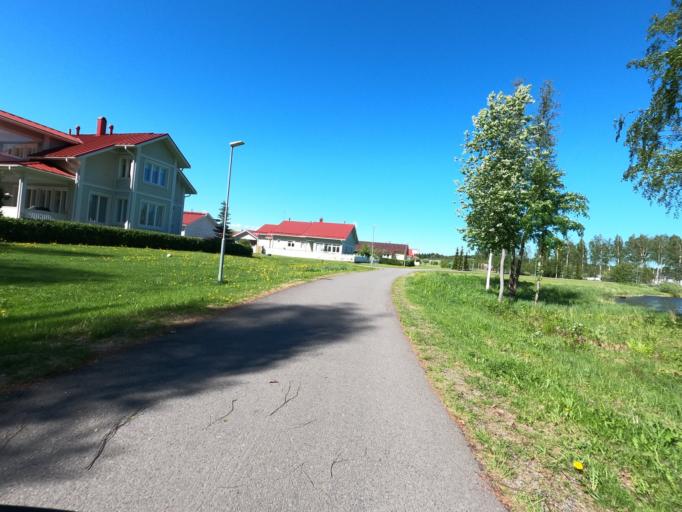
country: FI
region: North Karelia
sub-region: Joensuu
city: Joensuu
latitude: 62.5764
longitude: 29.7729
